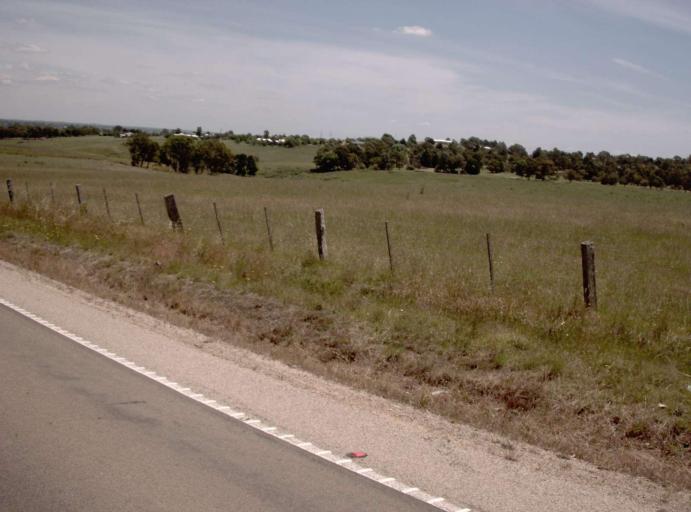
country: AU
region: Victoria
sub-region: East Gippsland
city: Bairnsdale
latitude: -37.8022
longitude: 147.6556
